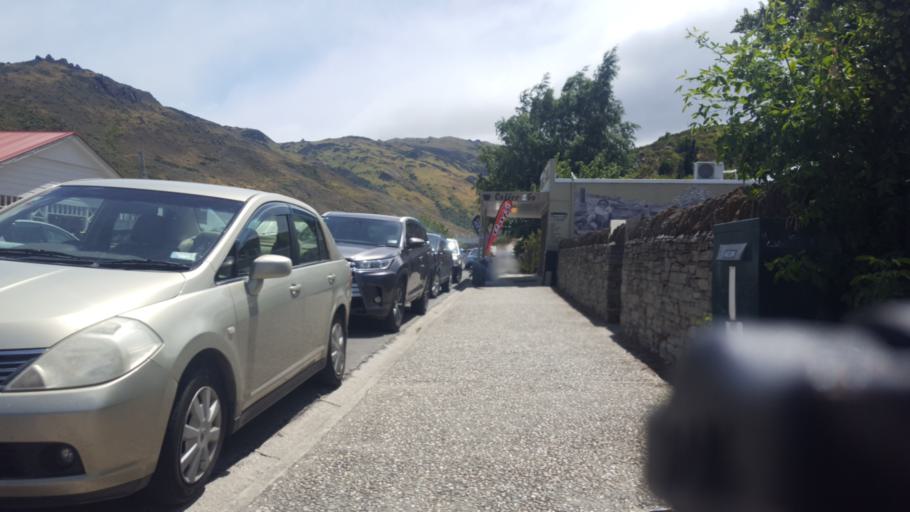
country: NZ
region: Otago
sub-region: Queenstown-Lakes District
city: Wanaka
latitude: -45.1863
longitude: 169.3156
